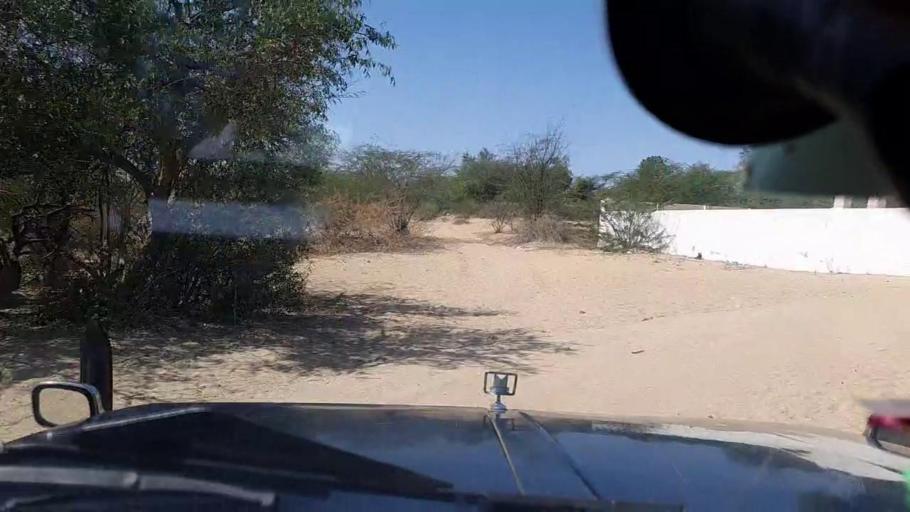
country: PK
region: Sindh
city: Mithi
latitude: 24.5934
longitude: 69.7062
